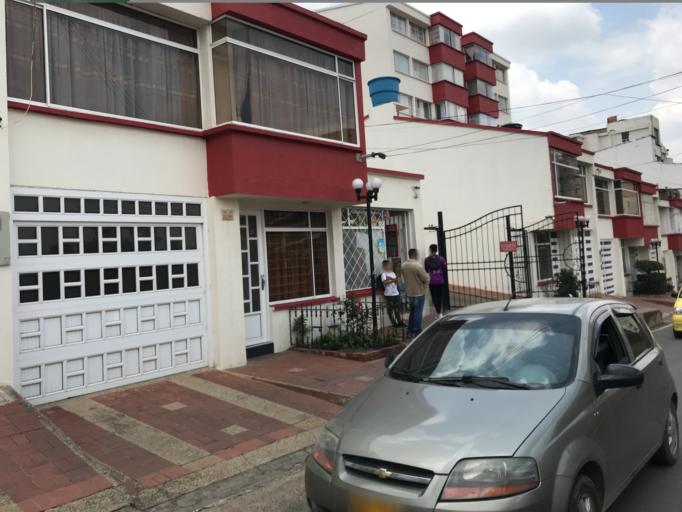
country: CO
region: Boyaca
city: Tunja
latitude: 5.5335
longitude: -73.3585
